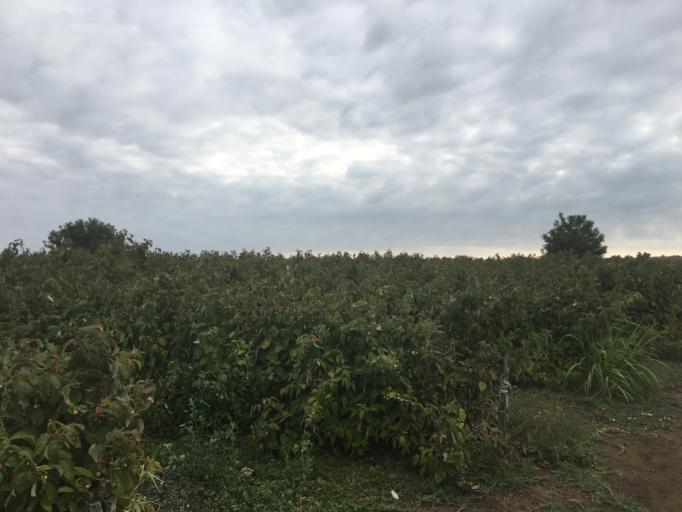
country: BG
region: Shumen
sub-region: Obshtina Veliki Preslav
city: Veliki Preslav
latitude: 43.1790
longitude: 26.8780
